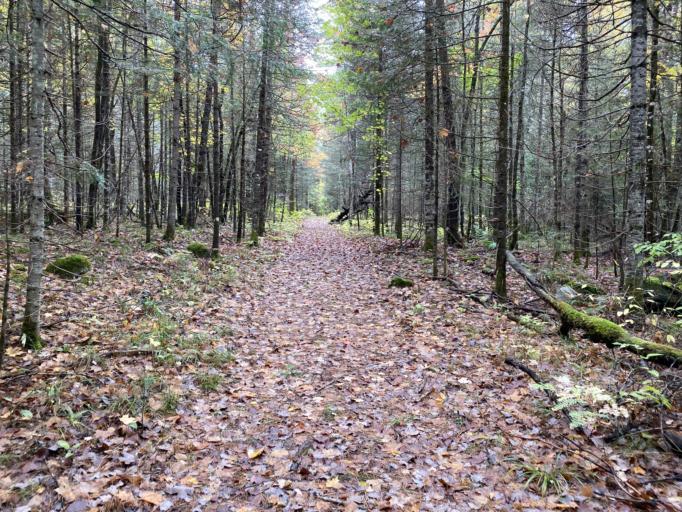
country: US
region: Michigan
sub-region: Marquette County
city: West Ishpeming
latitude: 46.5332
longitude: -87.9986
